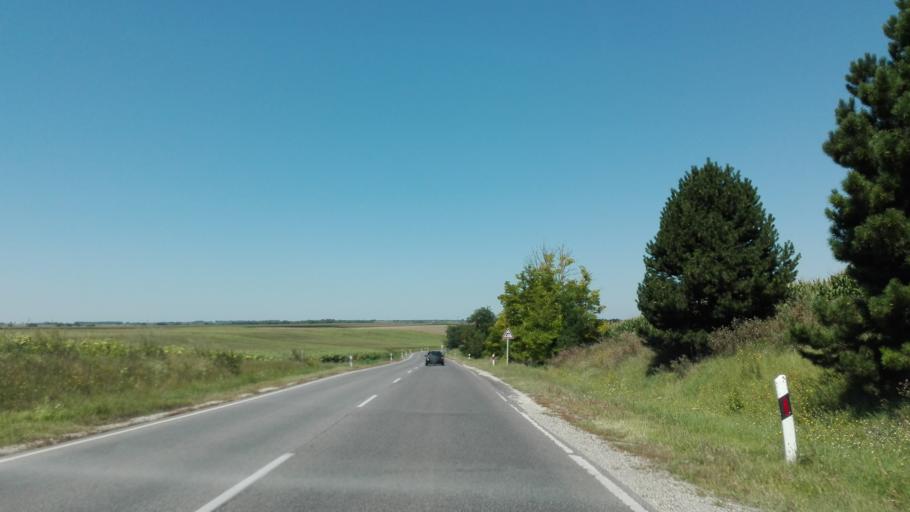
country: HU
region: Fejer
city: Deg
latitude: 46.8346
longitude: 18.4494
